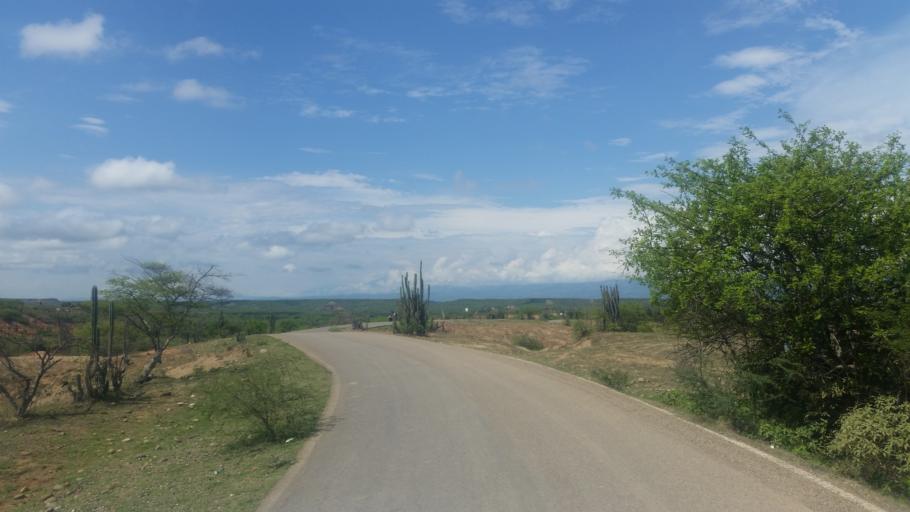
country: CO
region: Huila
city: Villavieja
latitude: 3.2338
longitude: -75.1734
